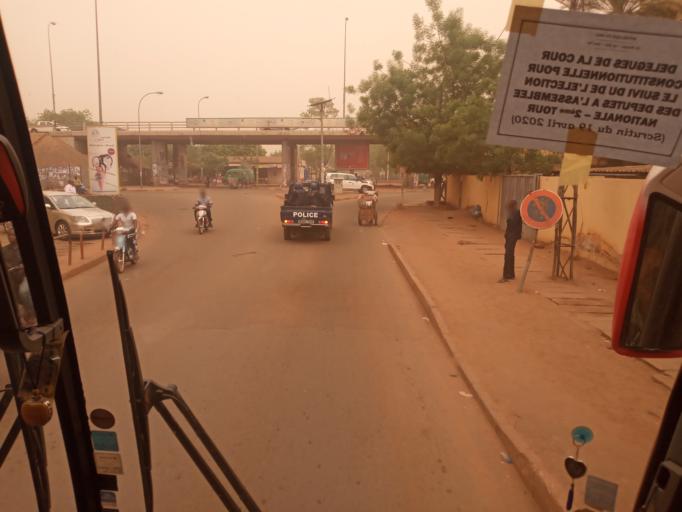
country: ML
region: Bamako
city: Bamako
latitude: 12.6484
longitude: -8.0080
